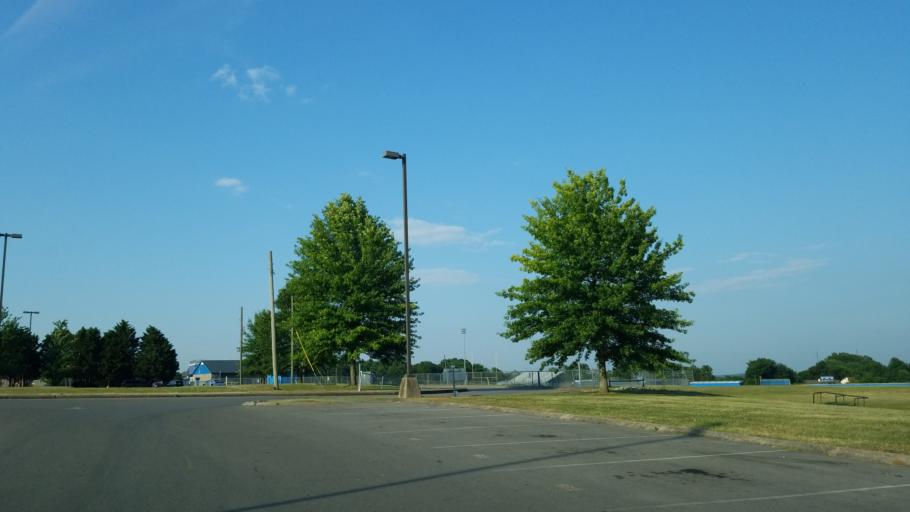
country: US
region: Tennessee
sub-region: Rutherford County
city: La Vergne
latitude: 36.0454
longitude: -86.5987
